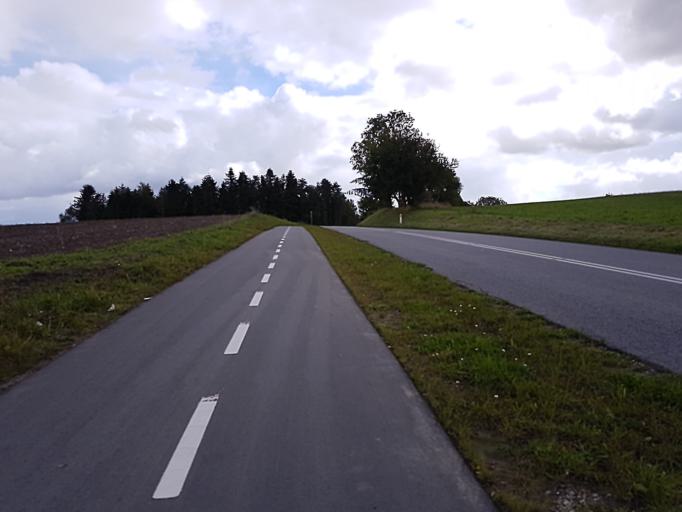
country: DK
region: Zealand
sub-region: Roskilde Kommune
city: Gundsomagle
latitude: 55.7482
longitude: 12.1411
